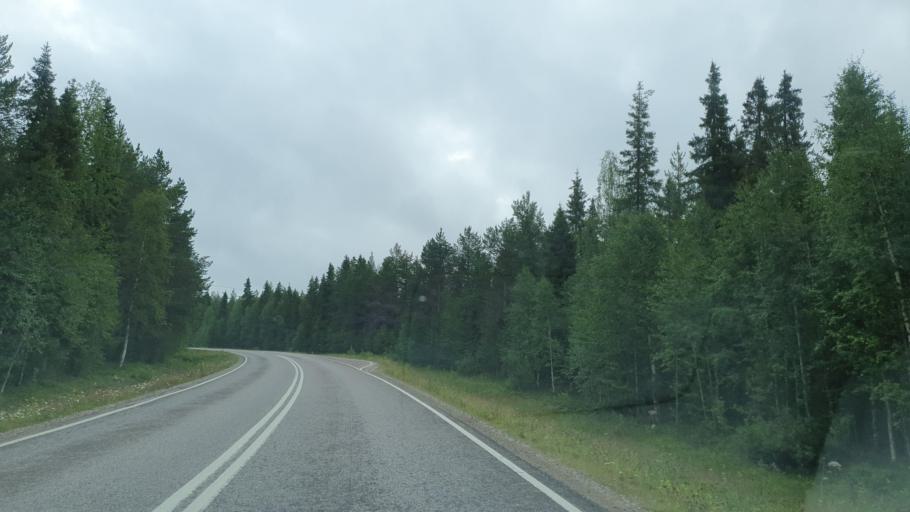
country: FI
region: Lapland
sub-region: Itae-Lappi
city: Pelkosenniemi
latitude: 66.9845
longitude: 27.5424
